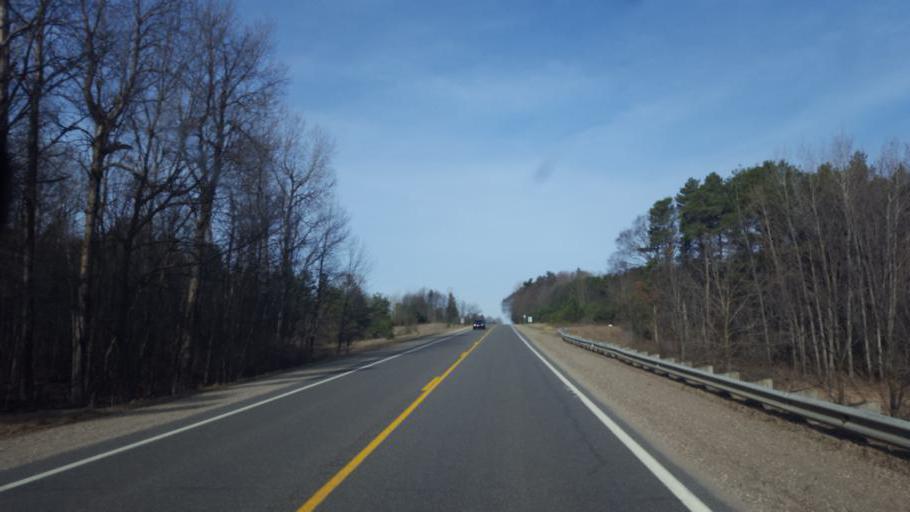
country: US
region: Michigan
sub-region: Montcalm County
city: Lakeview
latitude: 43.4320
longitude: -85.3384
